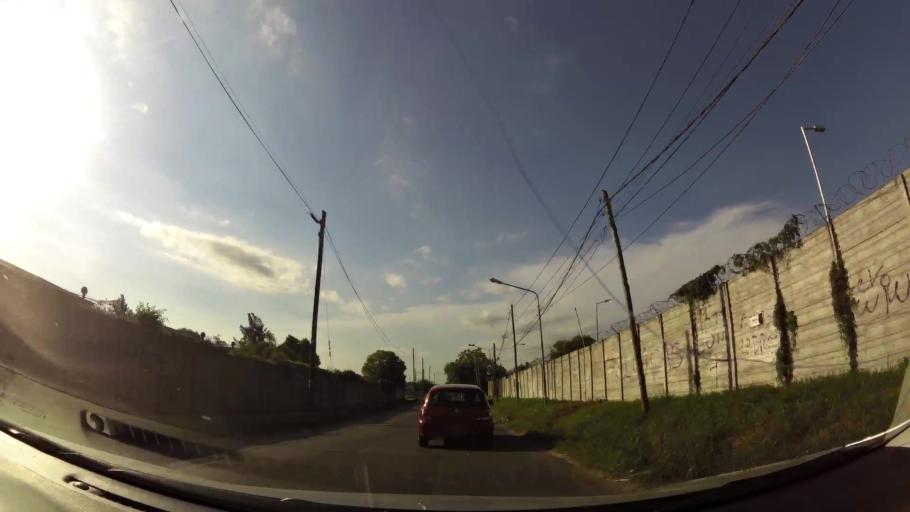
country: AR
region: Buenos Aires
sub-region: Partido de Tigre
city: Tigre
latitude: -34.4712
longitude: -58.6639
